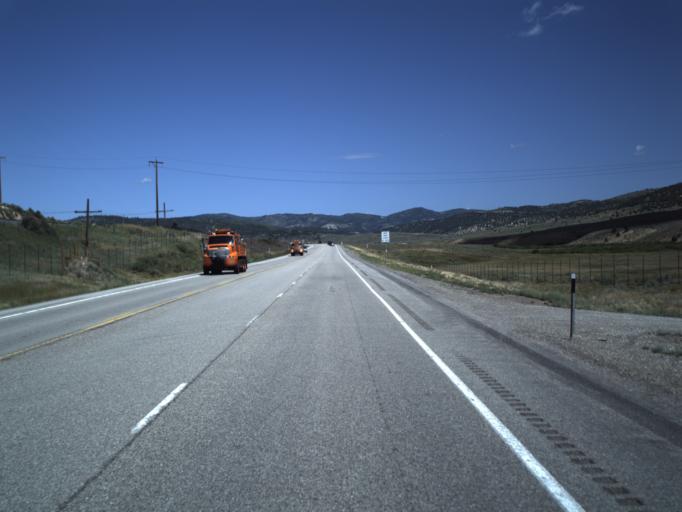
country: US
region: Utah
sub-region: Carbon County
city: Helper
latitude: 39.8881
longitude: -111.0503
